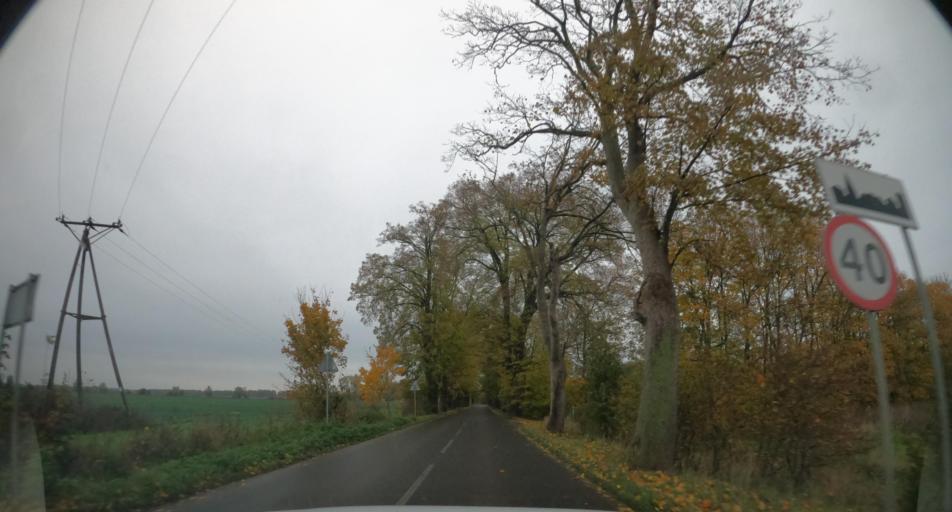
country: PL
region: West Pomeranian Voivodeship
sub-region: Powiat kamienski
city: Wolin
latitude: 53.8894
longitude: 14.6272
